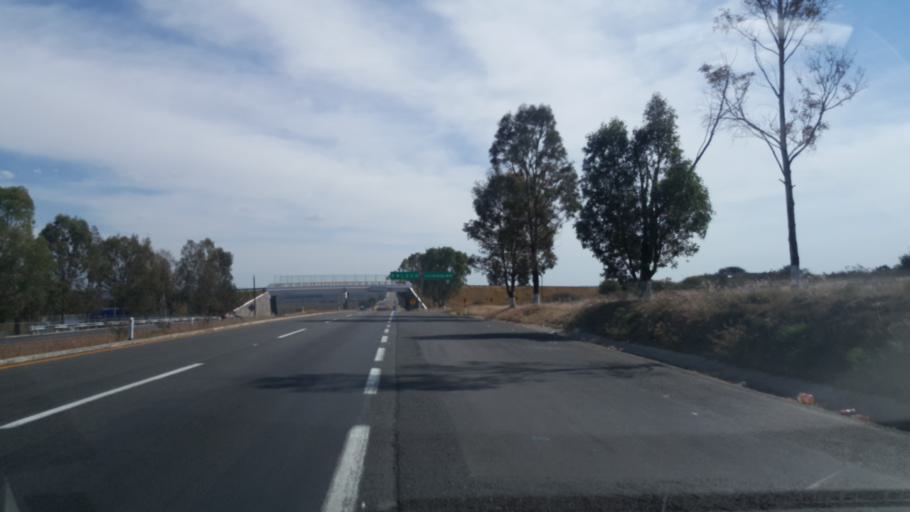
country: MX
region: Jalisco
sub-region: Lagos de Moreno
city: Cristeros [Fraccionamiento]
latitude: 21.2544
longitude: -101.9512
